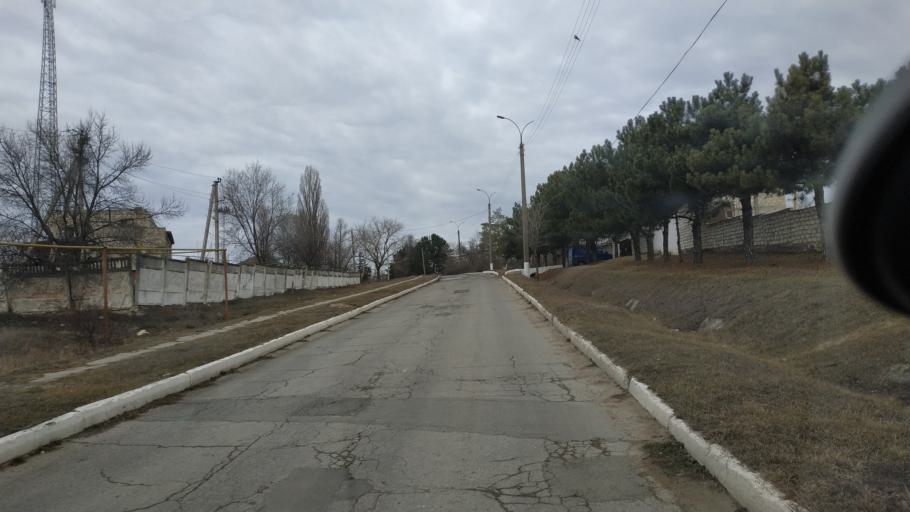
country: MD
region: Criuleni
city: Criuleni
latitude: 47.2195
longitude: 29.1571
